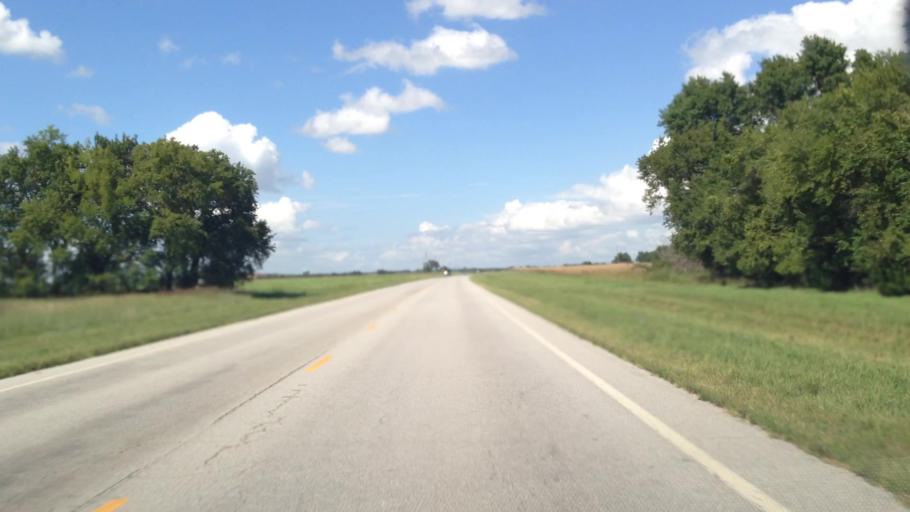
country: US
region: Kansas
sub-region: Labette County
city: Oswego
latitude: 37.1164
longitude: -95.1035
